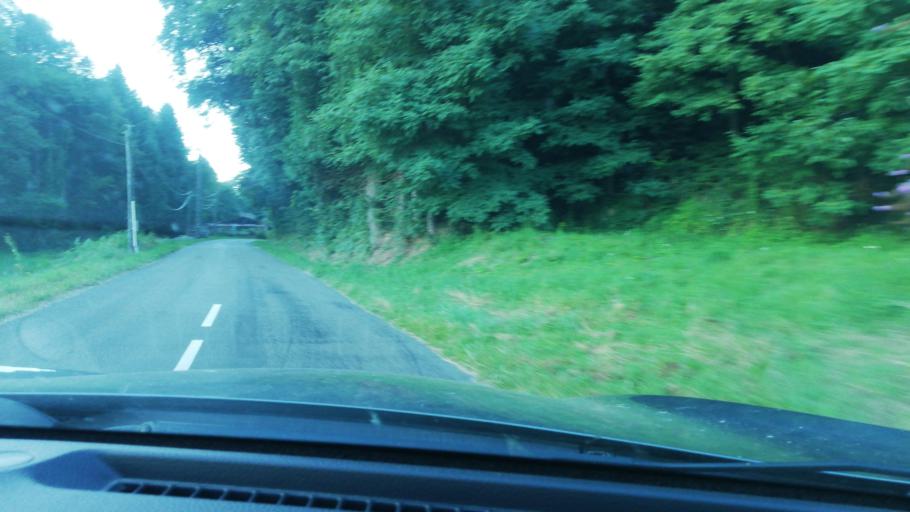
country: FR
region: Midi-Pyrenees
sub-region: Departement du Lot
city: Saint-Cere
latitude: 44.8776
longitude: 2.0300
